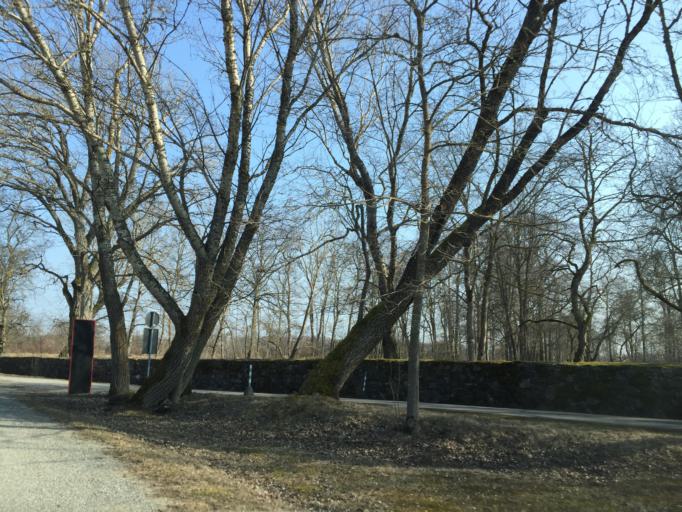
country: EE
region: Saare
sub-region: Orissaare vald
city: Orissaare
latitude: 58.5515
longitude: 23.2799
